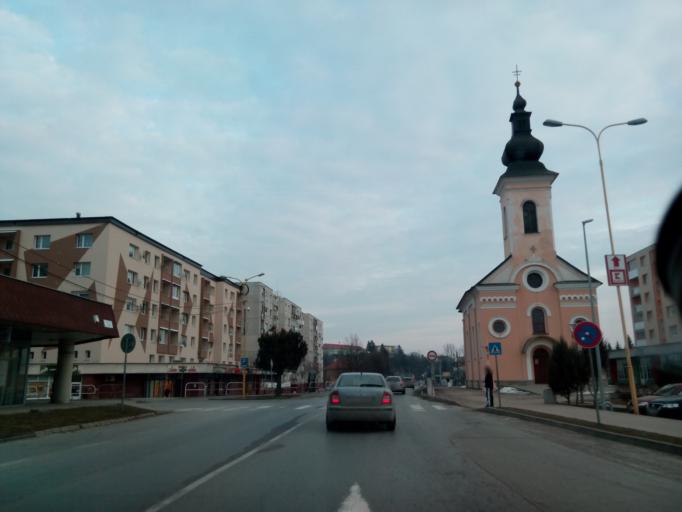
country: SK
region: Presovsky
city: Sabinov
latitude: 49.1014
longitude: 21.1016
